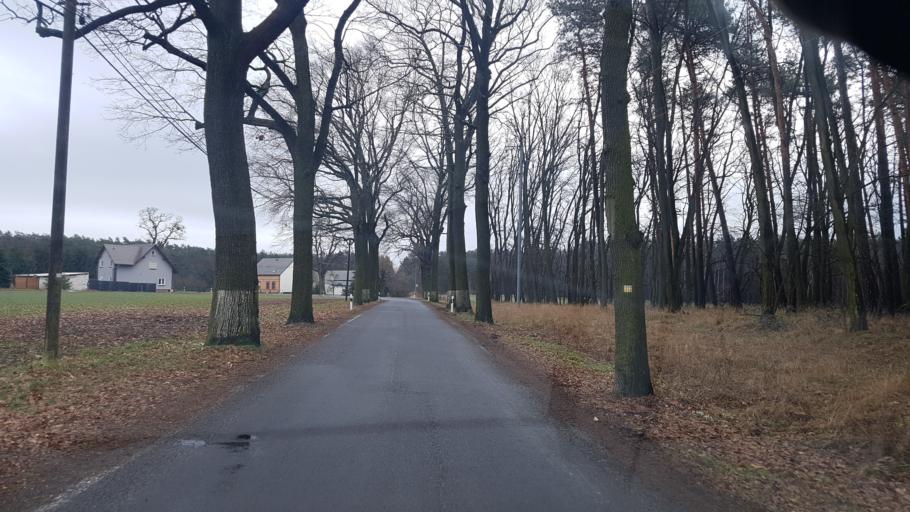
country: DE
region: Brandenburg
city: Neupetershain
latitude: 51.6186
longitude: 14.1075
